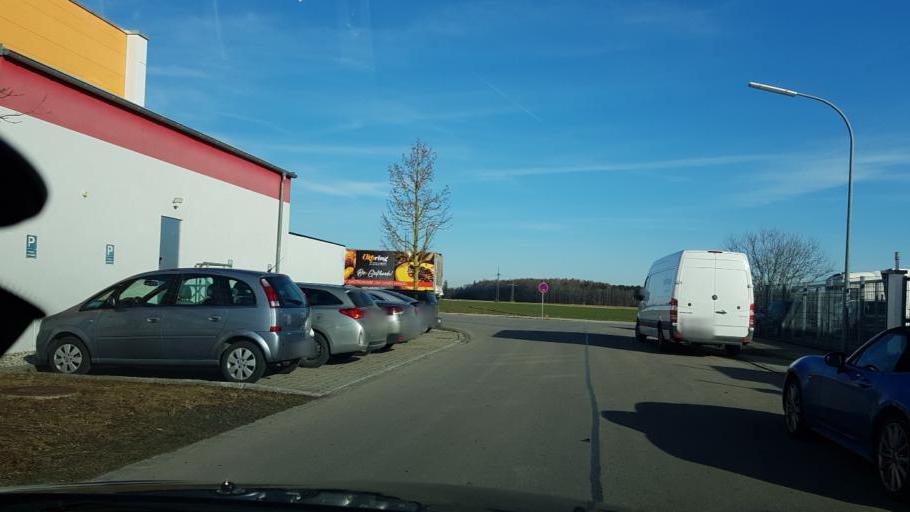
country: DE
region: Bavaria
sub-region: Upper Bavaria
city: Oberschweinbach
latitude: 48.2148
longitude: 11.1828
